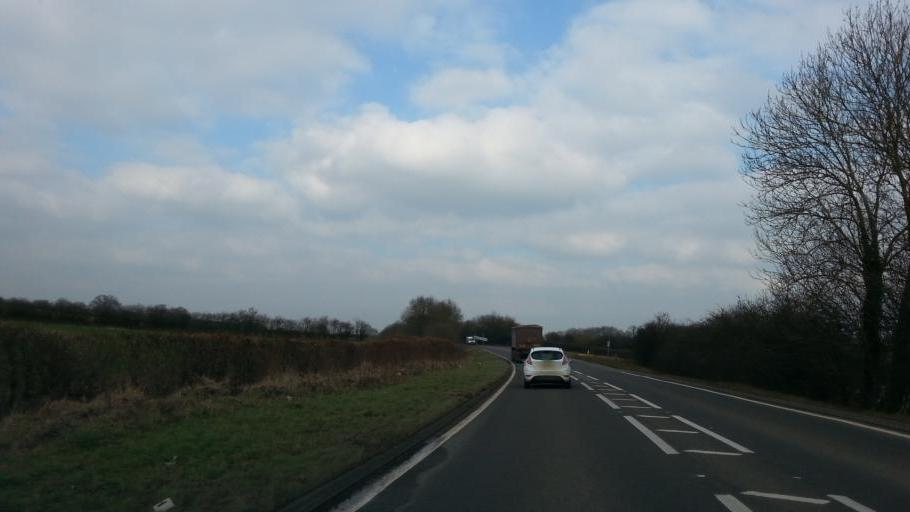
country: GB
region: England
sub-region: District of Rutland
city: South Luffenham
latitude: 52.5573
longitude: -0.5758
